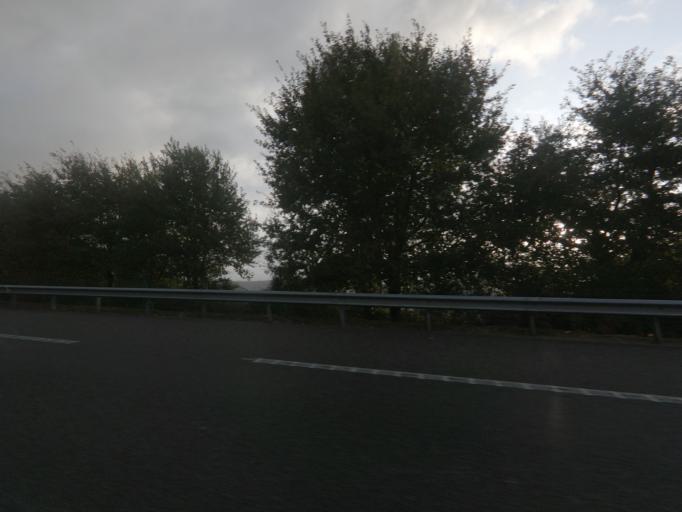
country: ES
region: Galicia
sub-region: Provincia de Pontevedra
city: Porrino
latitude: 42.1739
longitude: -8.6504
